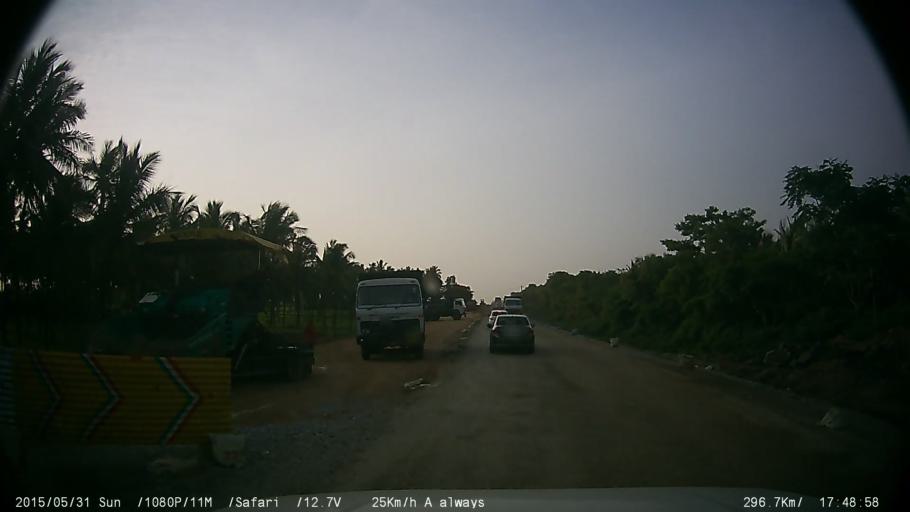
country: IN
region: Karnataka
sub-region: Mysore
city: Nanjangud
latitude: 11.9691
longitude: 76.6701
